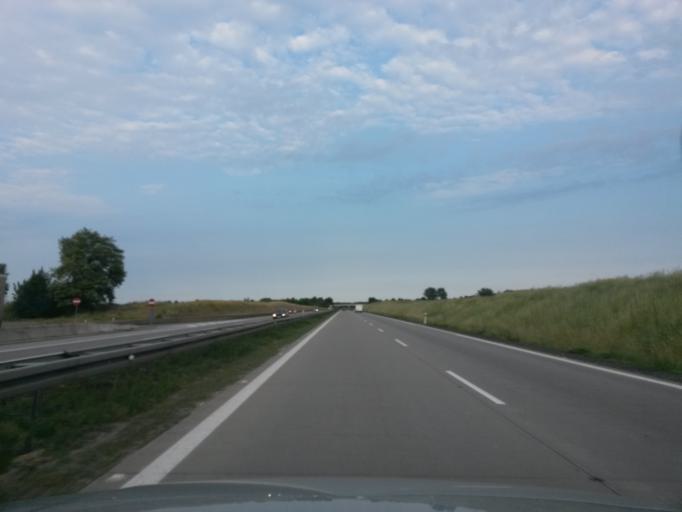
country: PL
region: Lower Silesian Voivodeship
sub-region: Powiat wroclawski
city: Katy Wroclawskie
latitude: 51.0302
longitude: 16.6493
